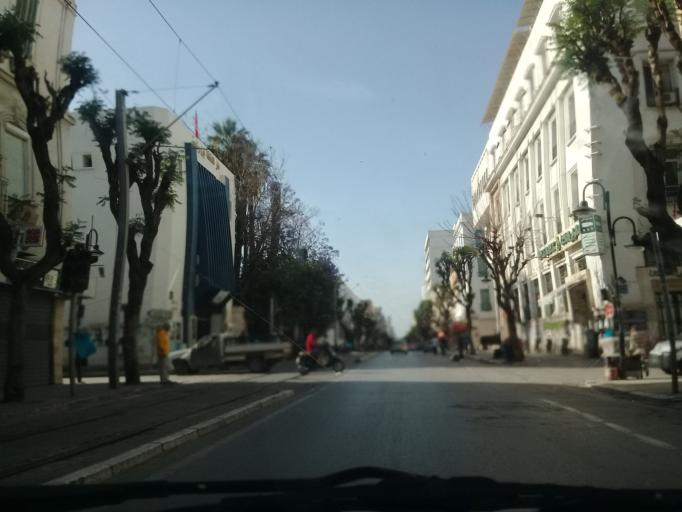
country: TN
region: Tunis
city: Tunis
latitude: 36.8009
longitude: 10.1812
